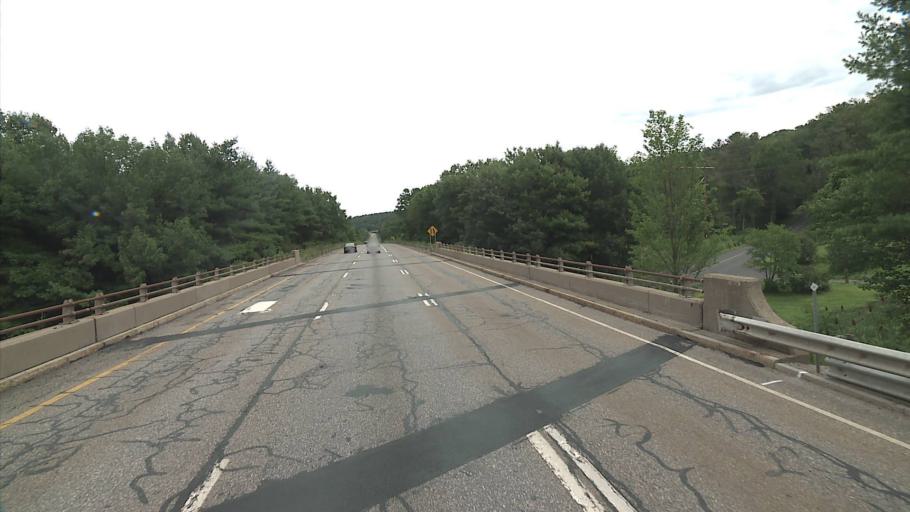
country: US
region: Connecticut
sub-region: Litchfield County
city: Torrington
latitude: 41.7774
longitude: -73.1126
